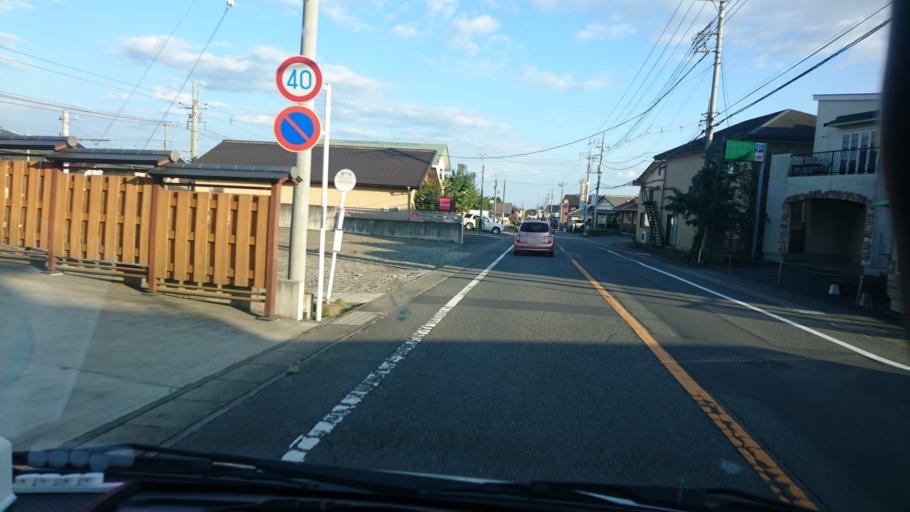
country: JP
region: Gunma
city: Omamacho-omama
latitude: 36.4222
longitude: 139.2927
